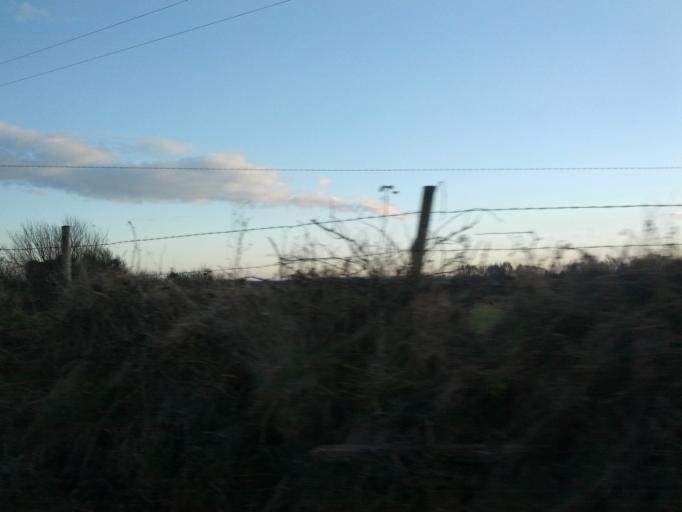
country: IE
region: Connaught
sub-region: County Galway
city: Athenry
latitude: 53.3260
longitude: -8.6325
